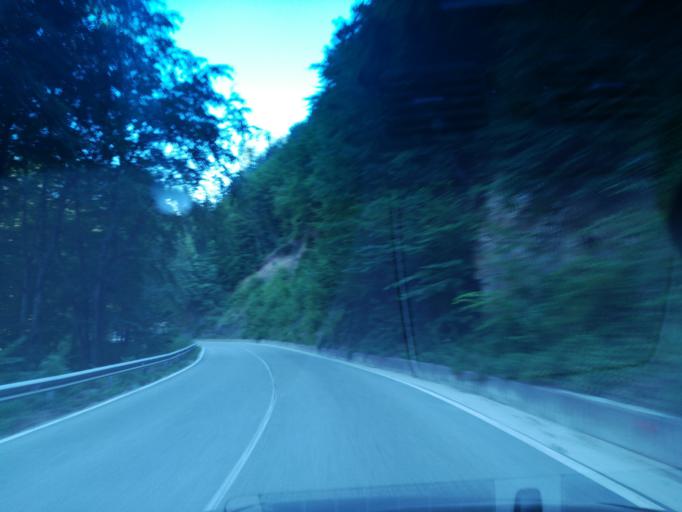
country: BG
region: Smolyan
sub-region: Obshtina Chepelare
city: Chepelare
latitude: 41.8110
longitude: 24.7054
